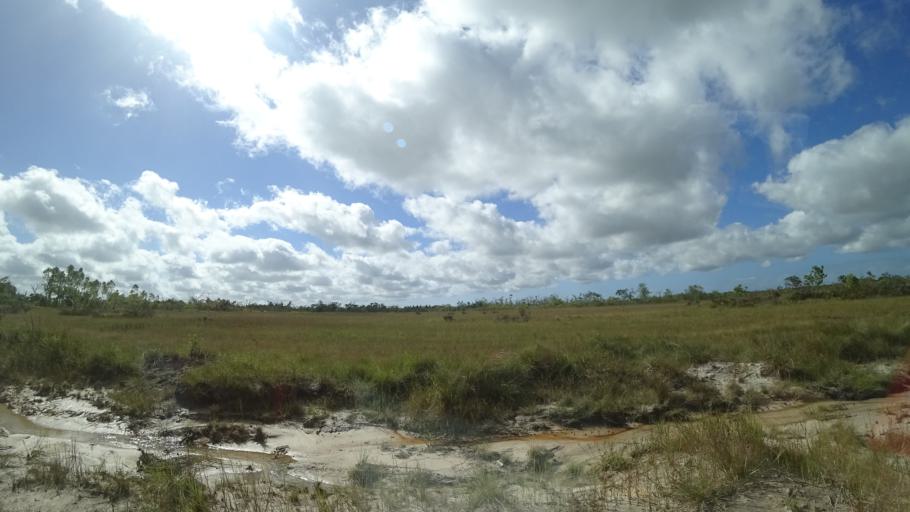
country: MZ
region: Sofala
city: Dondo
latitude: -19.5770
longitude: 35.0869
